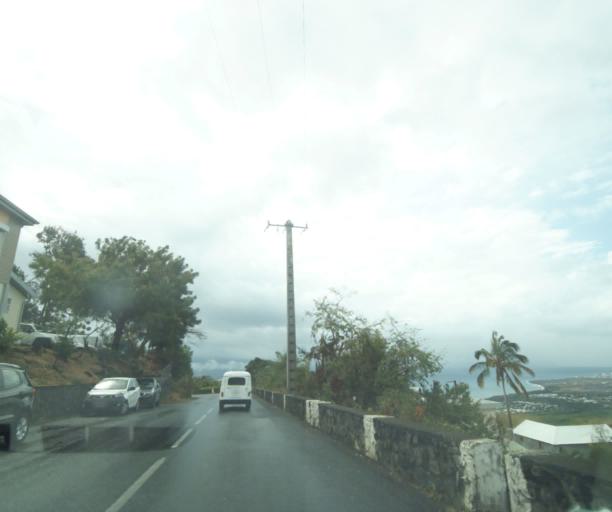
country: RE
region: Reunion
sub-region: Reunion
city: Saint-Paul
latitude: -21.0230
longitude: 55.2927
